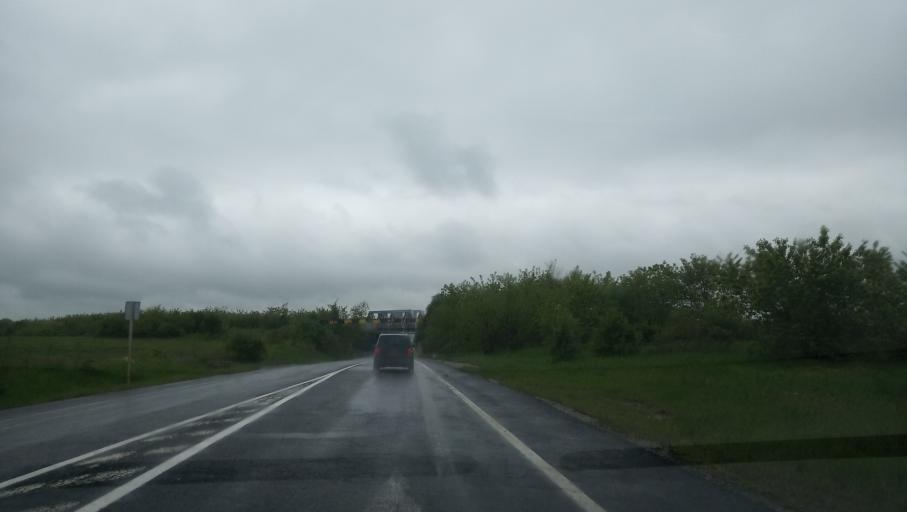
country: RO
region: Sibiu
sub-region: Oras Miercurea Sibiului
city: Miercurea Sibiului
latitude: 45.8641
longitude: 23.8107
